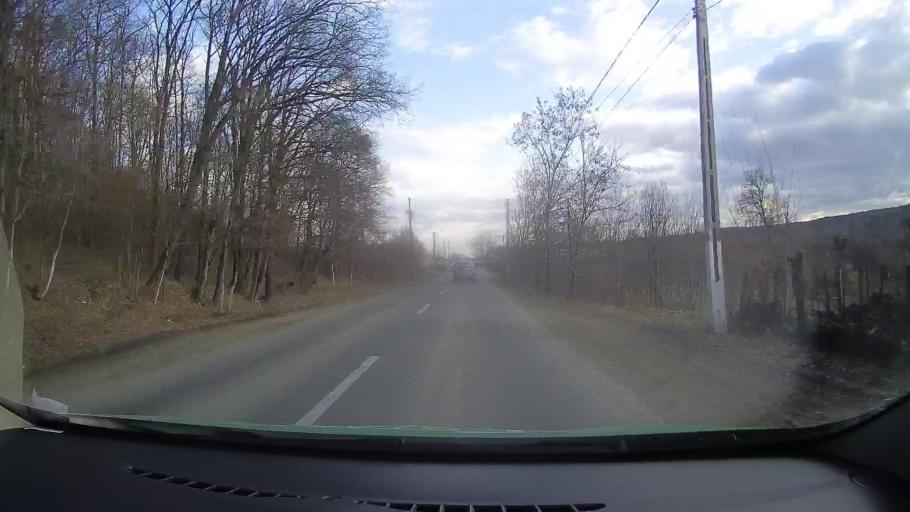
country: RO
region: Dambovita
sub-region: Comuna Gura Ocnitei
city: Gura Ocnitei
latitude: 44.9546
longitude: 25.5537
